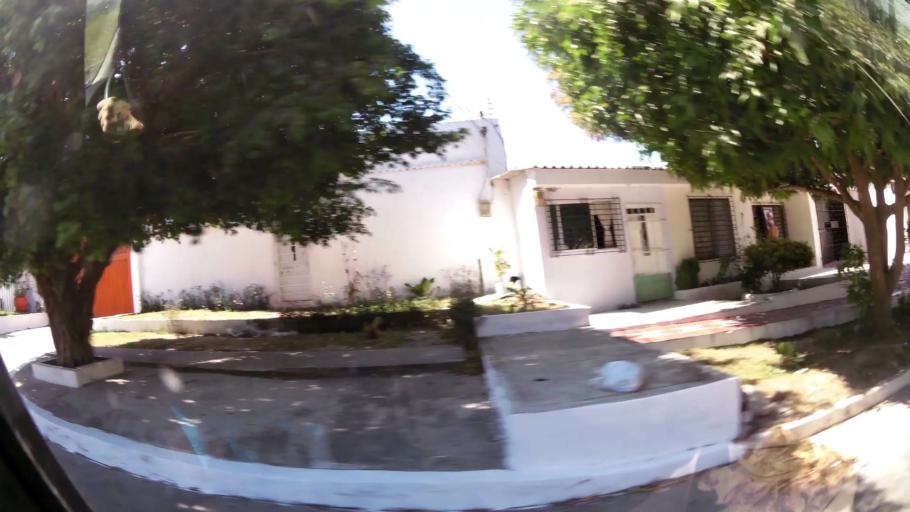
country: CO
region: Atlantico
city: Barranquilla
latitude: 11.0043
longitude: -74.7906
